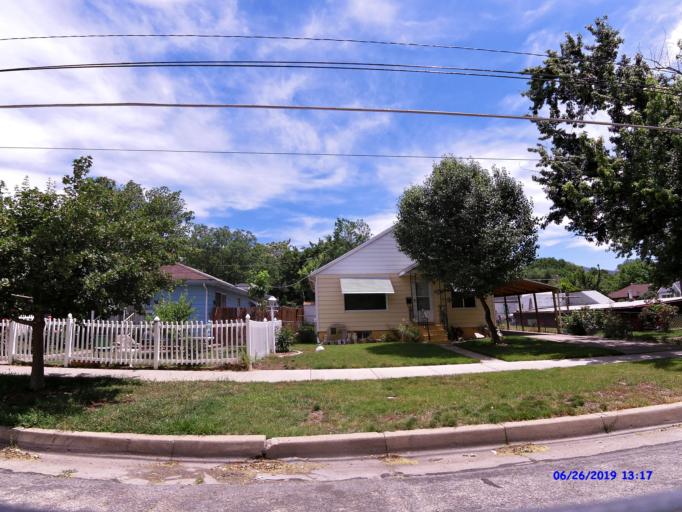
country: US
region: Utah
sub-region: Weber County
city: Ogden
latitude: 41.2084
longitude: -111.9652
